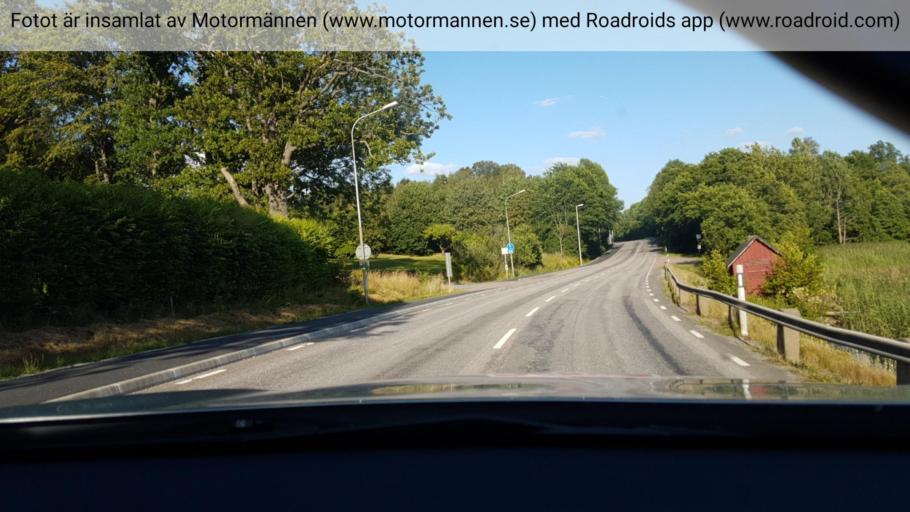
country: SE
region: Vaestra Goetaland
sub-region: Harryda Kommun
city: Landvetter
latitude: 57.6858
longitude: 12.1930
